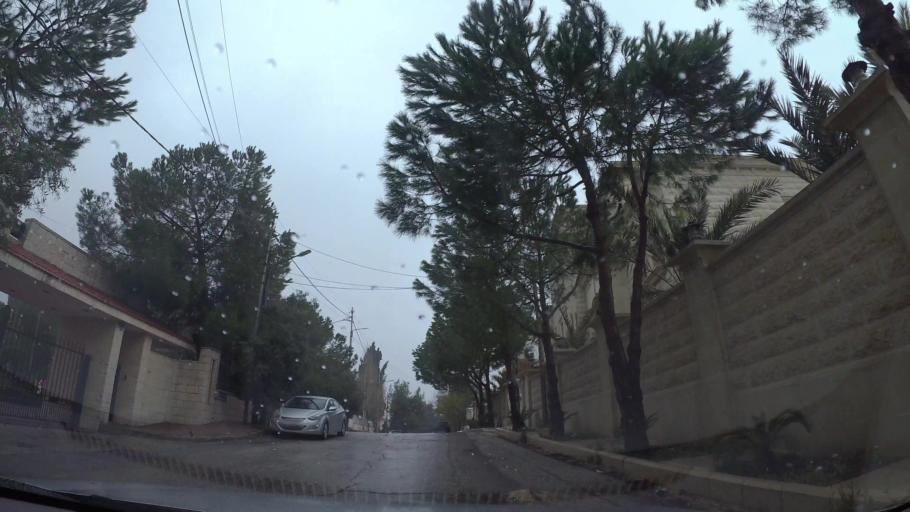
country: JO
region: Amman
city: Al Jubayhah
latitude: 31.9983
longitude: 35.8283
